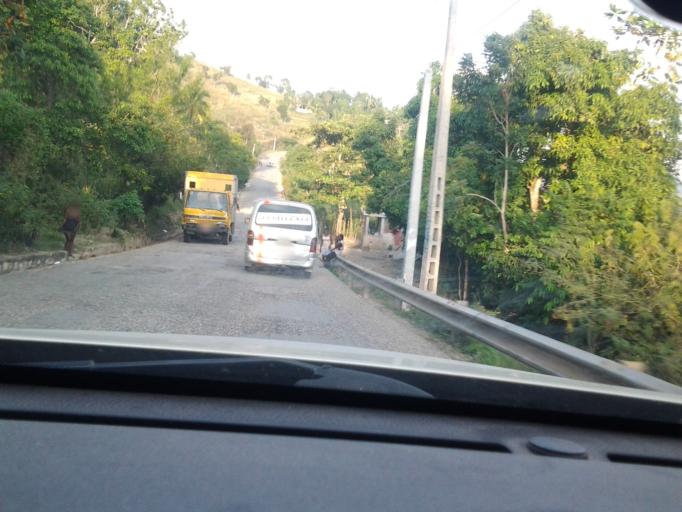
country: HT
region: Sud-Est
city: Jacmel
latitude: 18.3248
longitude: -72.5805
